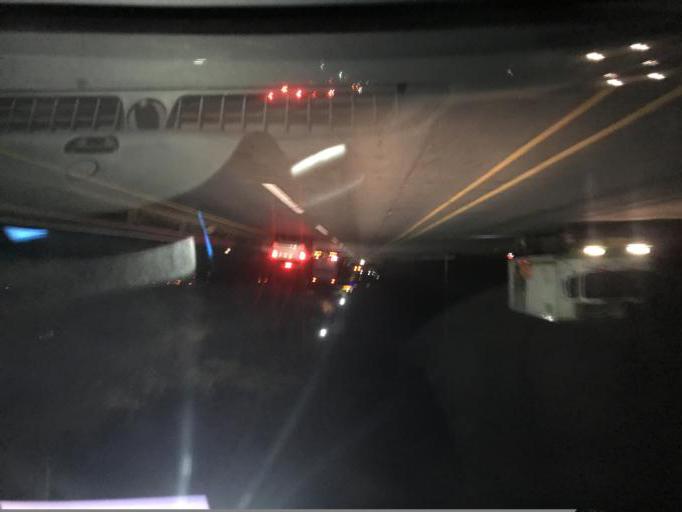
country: KR
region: Daegu
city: Hwawon
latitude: 35.7297
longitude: 128.4718
